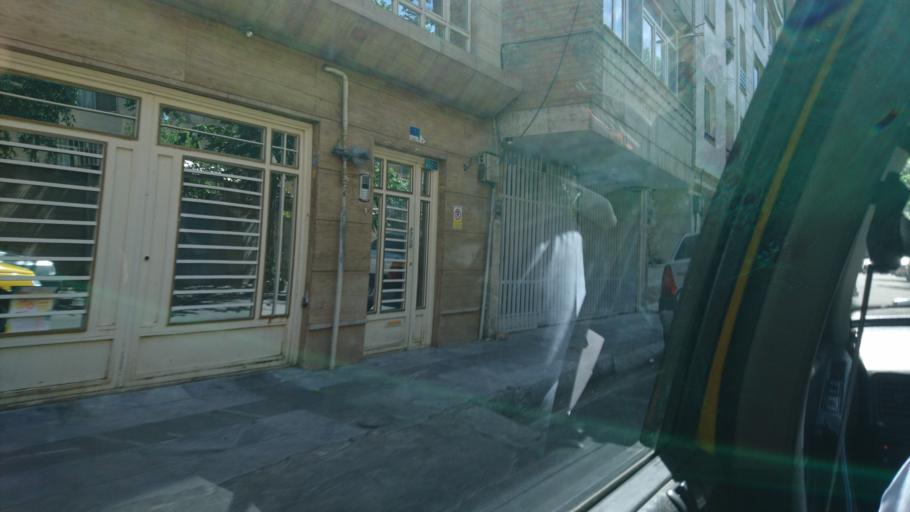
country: IR
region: Tehran
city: Tehran
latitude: 35.7028
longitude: 51.3909
